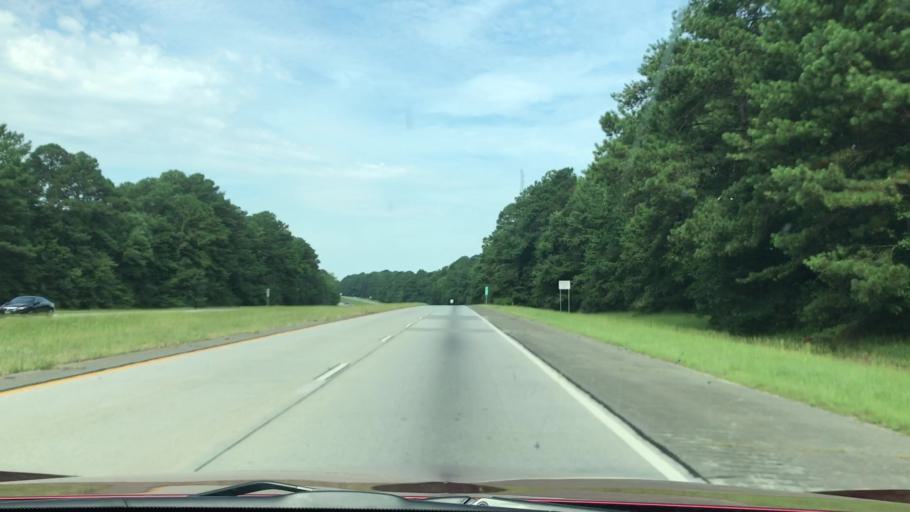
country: US
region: Georgia
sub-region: Warren County
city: Firing Range
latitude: 33.5039
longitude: -82.7650
